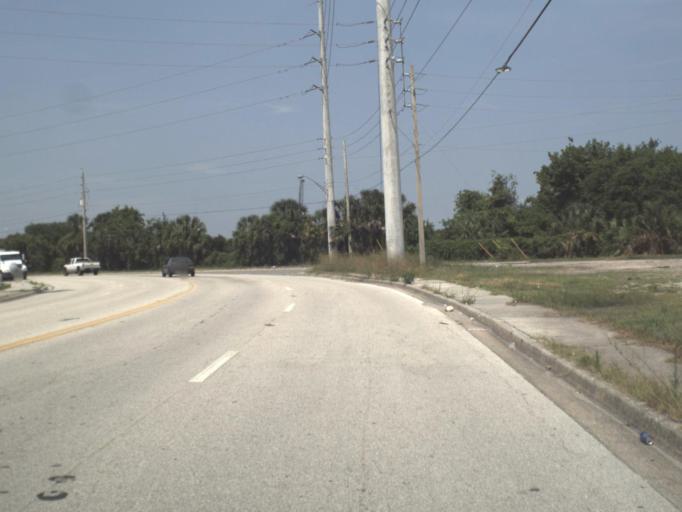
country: US
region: Florida
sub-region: Duval County
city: Jacksonville
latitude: 30.3417
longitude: -81.6288
